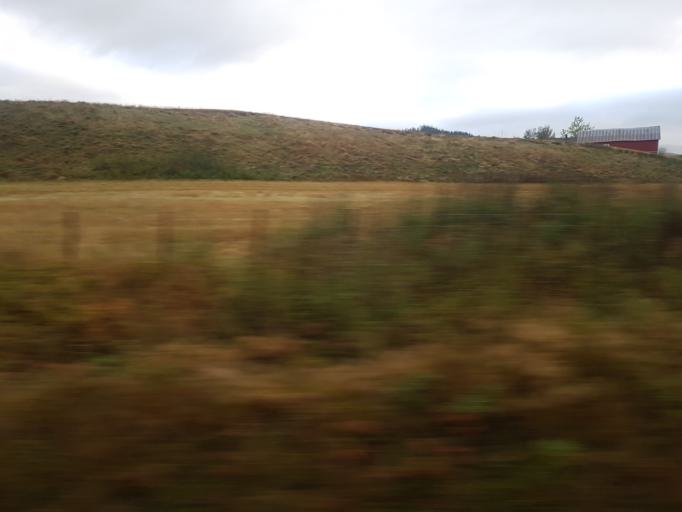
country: NO
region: Sor-Trondelag
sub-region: Melhus
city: Lundamo
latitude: 63.1908
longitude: 10.3081
